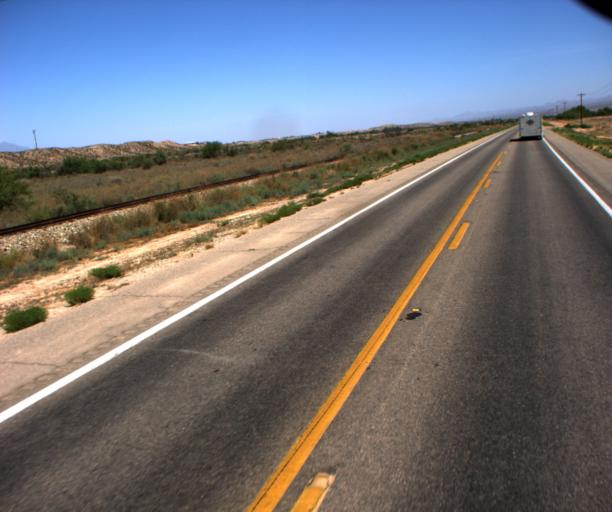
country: US
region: Arizona
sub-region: Graham County
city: Pima
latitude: 32.9931
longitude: -109.9388
